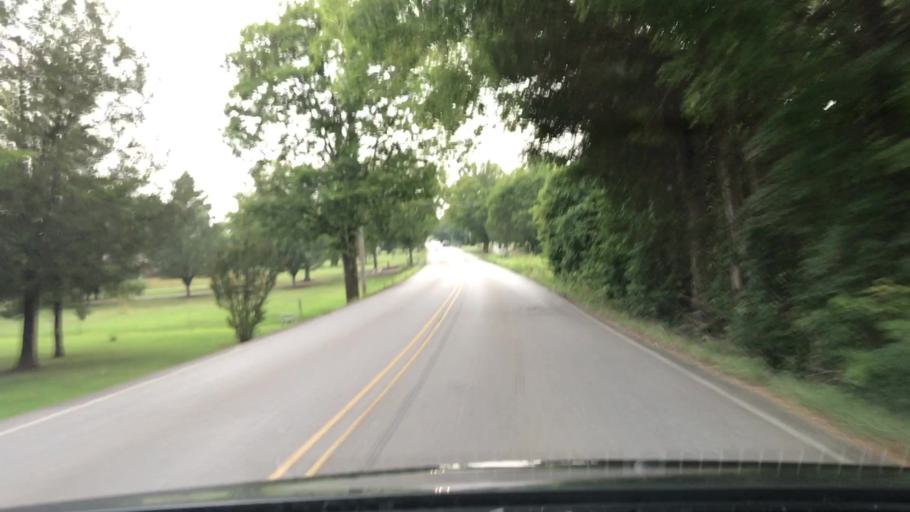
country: US
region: Tennessee
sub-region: Williamson County
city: Nolensville
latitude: 35.9524
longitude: -86.6528
